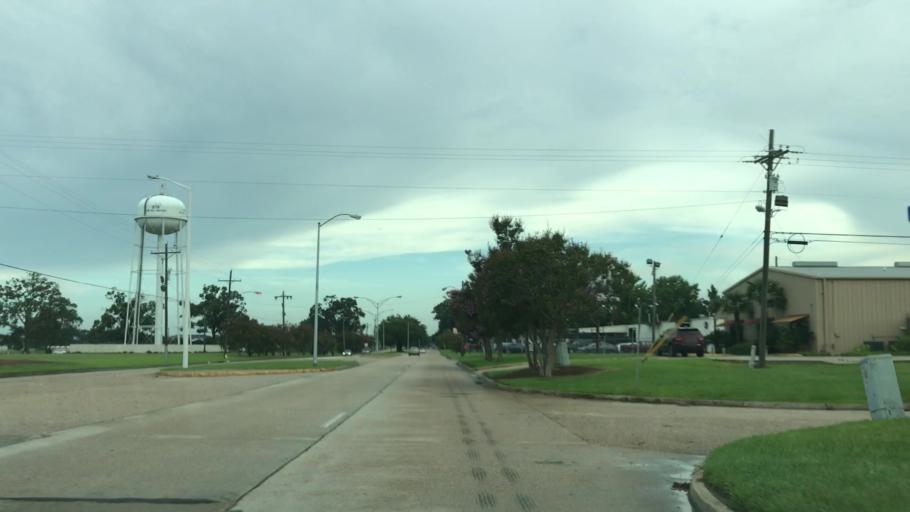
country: US
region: Louisiana
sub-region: East Baton Rouge Parish
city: Brownsfield
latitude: 30.5323
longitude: -91.1614
